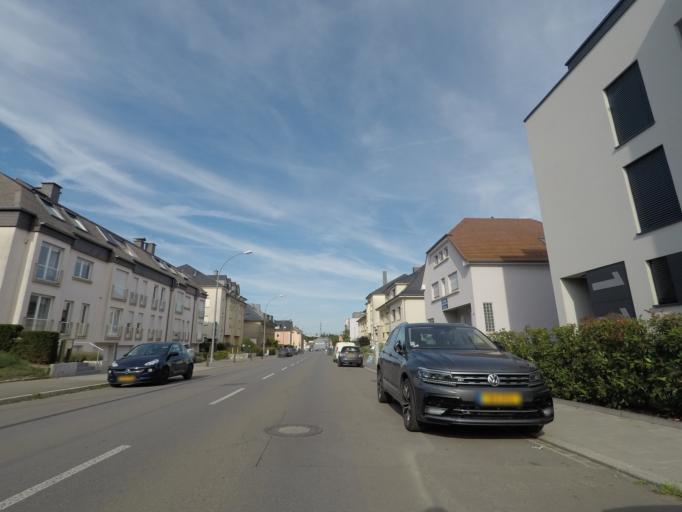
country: LU
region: Luxembourg
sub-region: Canton de Luxembourg
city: Luxembourg
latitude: 49.5937
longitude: 6.1084
